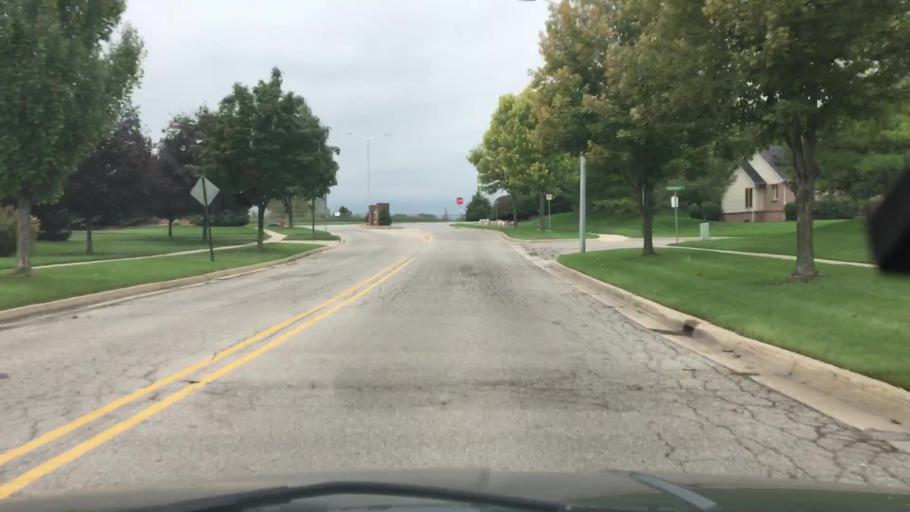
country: US
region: Michigan
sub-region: Livingston County
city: Brighton
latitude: 42.5082
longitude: -83.7837
